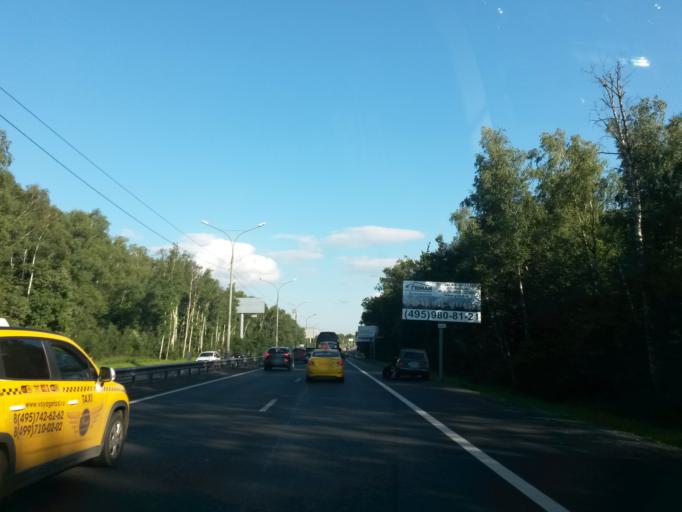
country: RU
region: Moskovskaya
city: Petrovskaya
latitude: 55.5385
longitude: 37.8063
